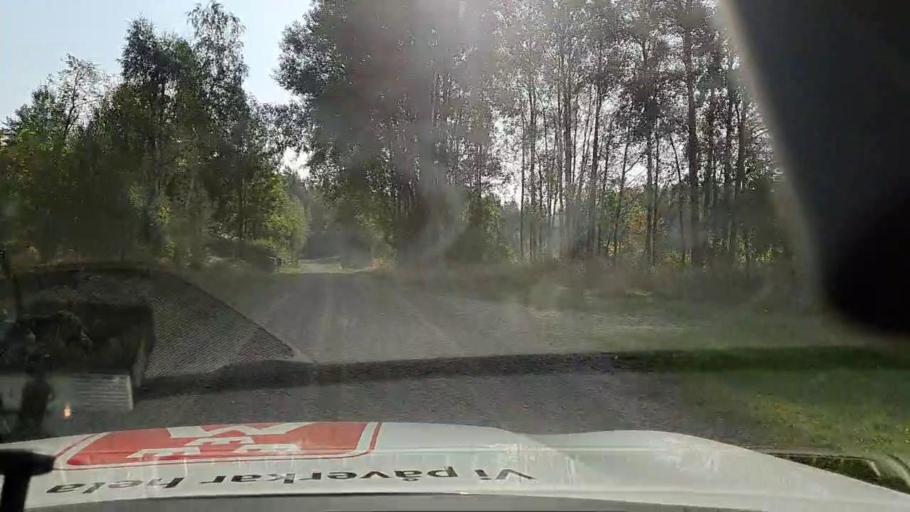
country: SE
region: Vaestmanland
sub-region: Kungsors Kommun
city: Kungsoer
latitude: 59.3497
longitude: 16.1656
